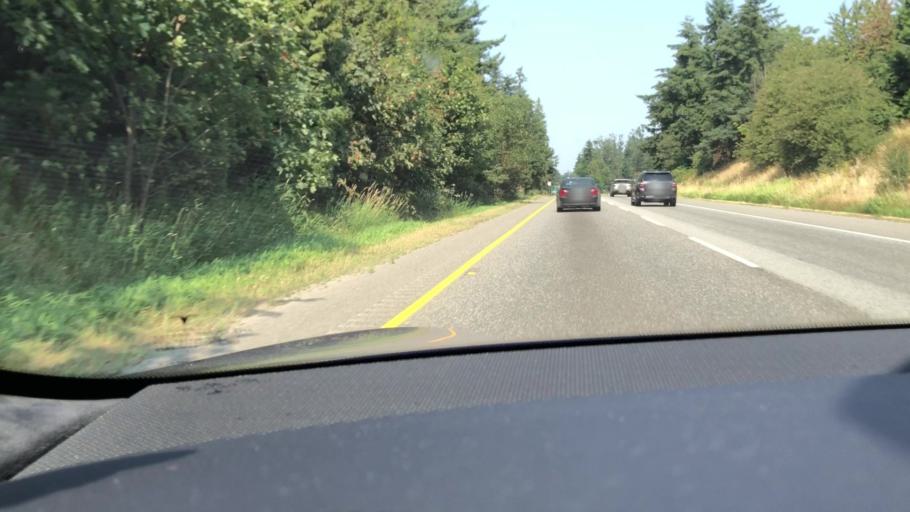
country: US
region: Washington
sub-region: Whatcom County
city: Sumas
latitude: 49.0430
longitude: -122.3471
